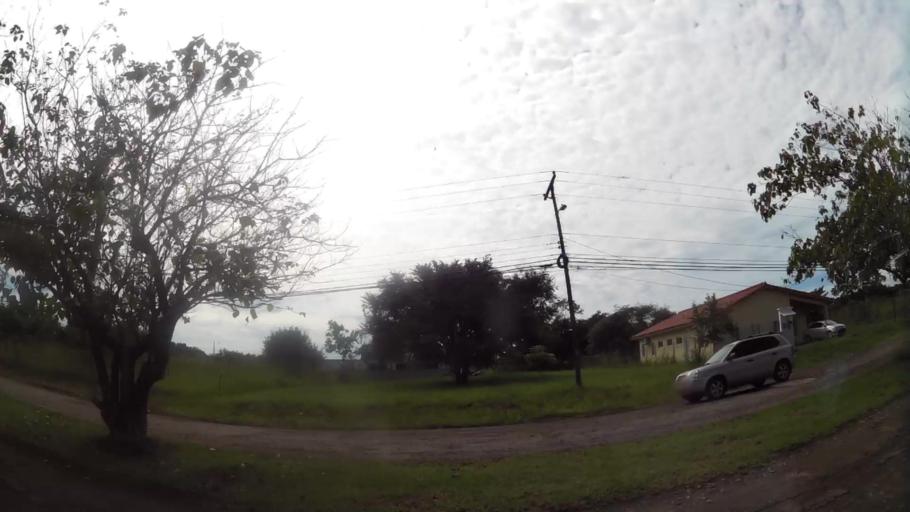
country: PA
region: Panama
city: Nueva Gorgona
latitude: 8.5456
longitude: -79.8978
